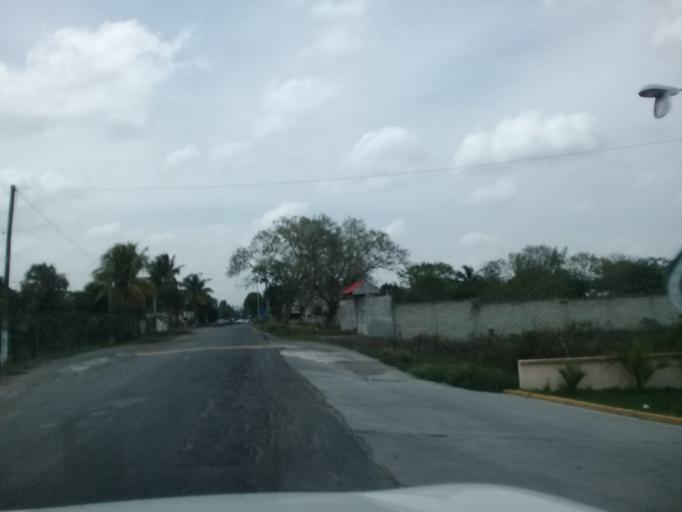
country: MX
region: Veracruz
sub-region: Emiliano Zapata
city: Plan del Rio
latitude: 19.3564
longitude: -96.6585
